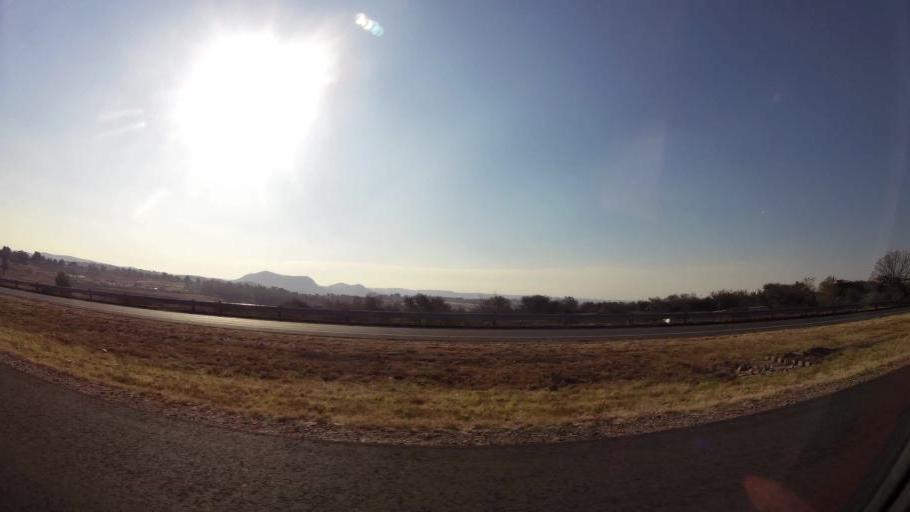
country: ZA
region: Gauteng
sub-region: West Rand District Municipality
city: Muldersdriseloop
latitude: -26.0178
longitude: 27.8655
